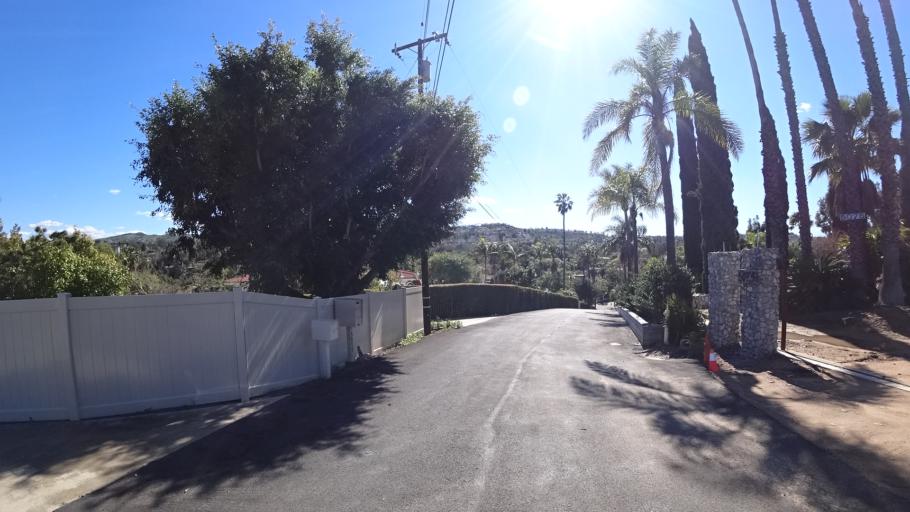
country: US
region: California
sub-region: Orange County
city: Villa Park
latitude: 33.8491
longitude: -117.8062
